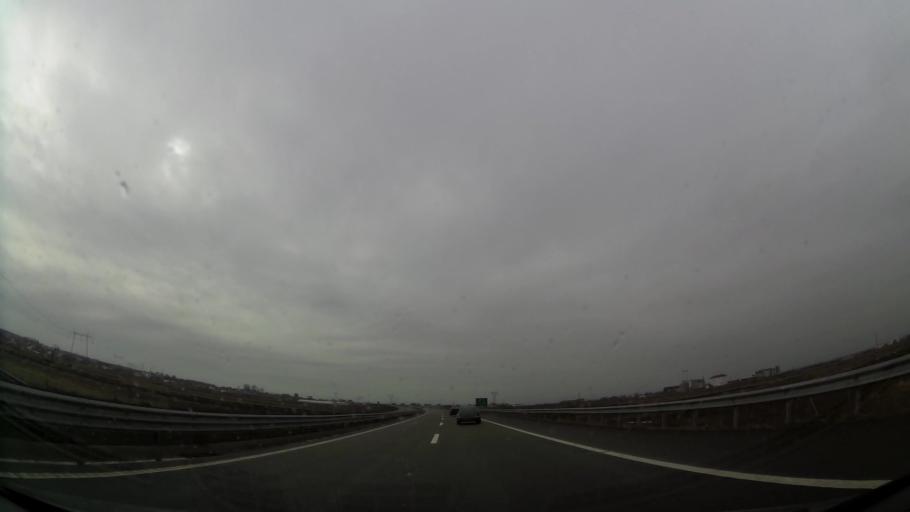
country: XK
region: Pristina
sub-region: Lipjan
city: Lipljan
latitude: 42.4820
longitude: 21.1869
